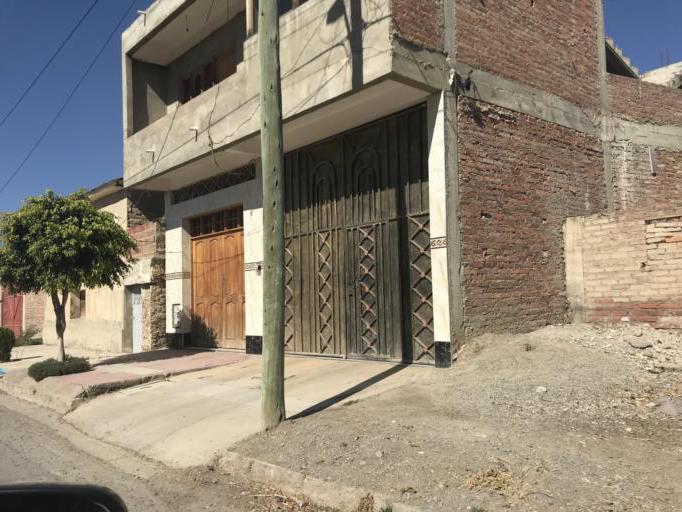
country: BO
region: Cochabamba
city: Punata
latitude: -17.5504
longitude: -65.8479
